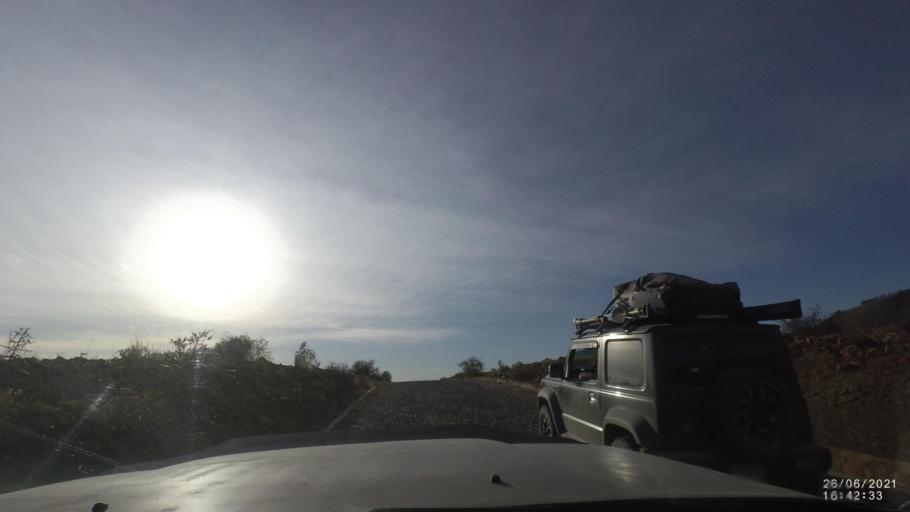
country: BO
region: Cochabamba
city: Arani
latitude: -17.7638
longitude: -65.8272
